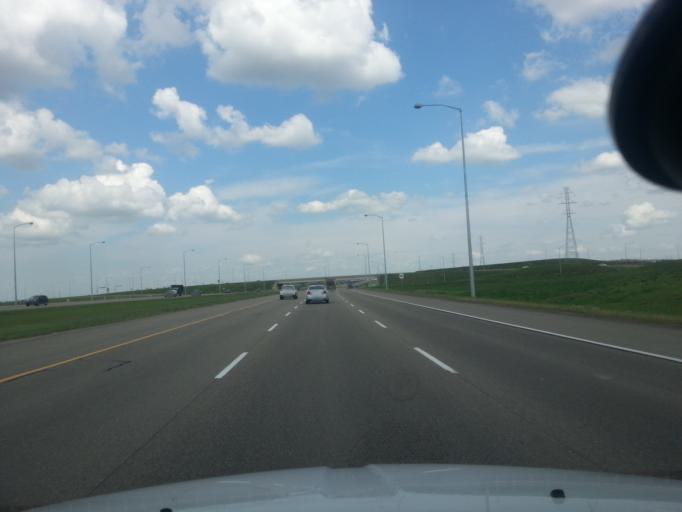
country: CA
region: Alberta
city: St. Albert
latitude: 53.5878
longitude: -113.6512
